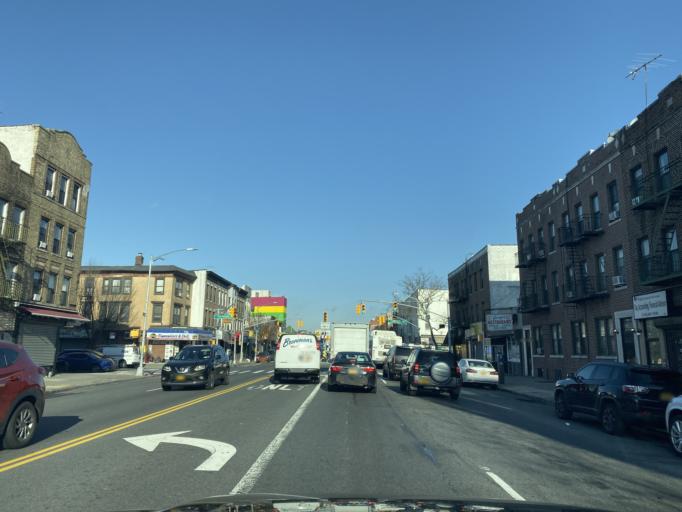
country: US
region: New York
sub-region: Kings County
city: Brooklyn
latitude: 40.6386
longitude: -73.9686
